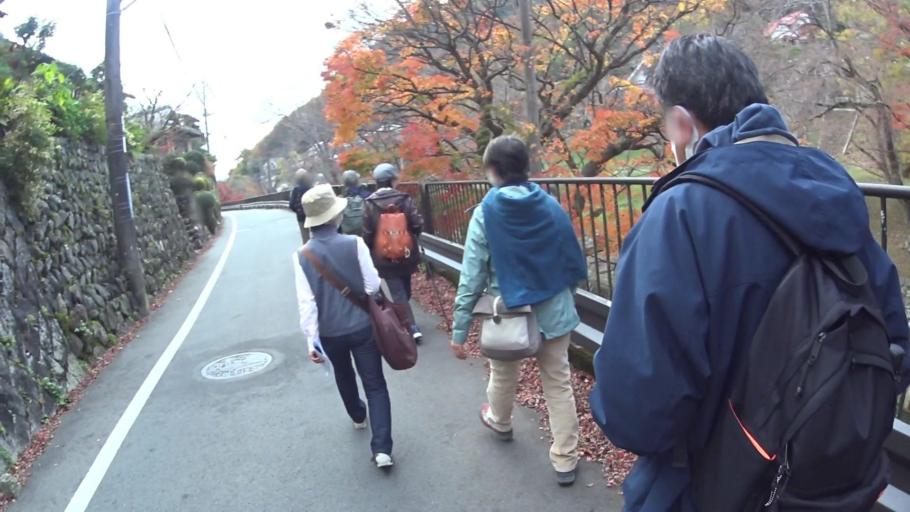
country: JP
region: Shiga Prefecture
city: Otsu-shi
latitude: 34.9980
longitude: 135.8311
